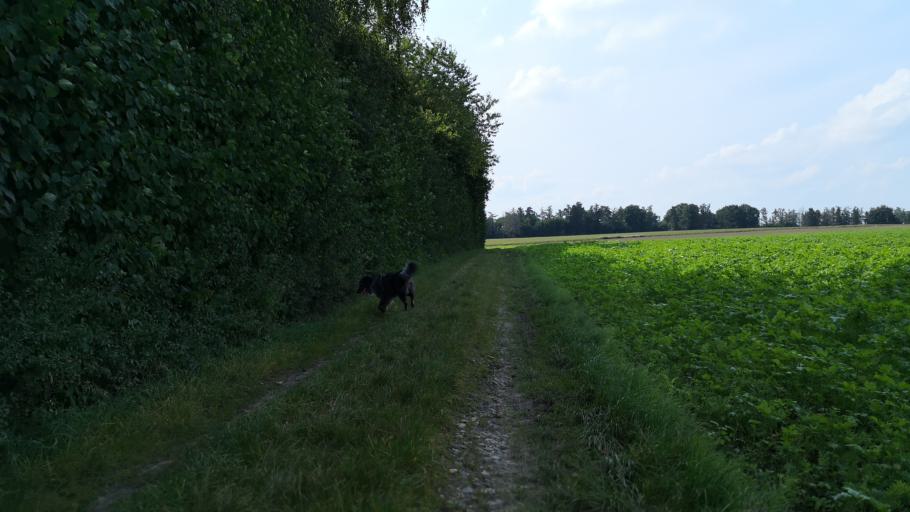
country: DE
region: Bavaria
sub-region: Upper Bavaria
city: Poing
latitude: 48.1787
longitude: 11.8202
